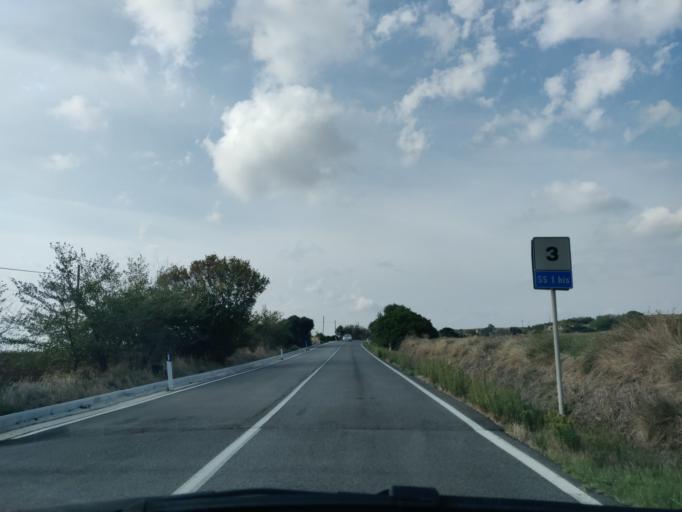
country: IT
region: Latium
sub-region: Provincia di Viterbo
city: Tarquinia
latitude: 42.2310
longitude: 11.7963
